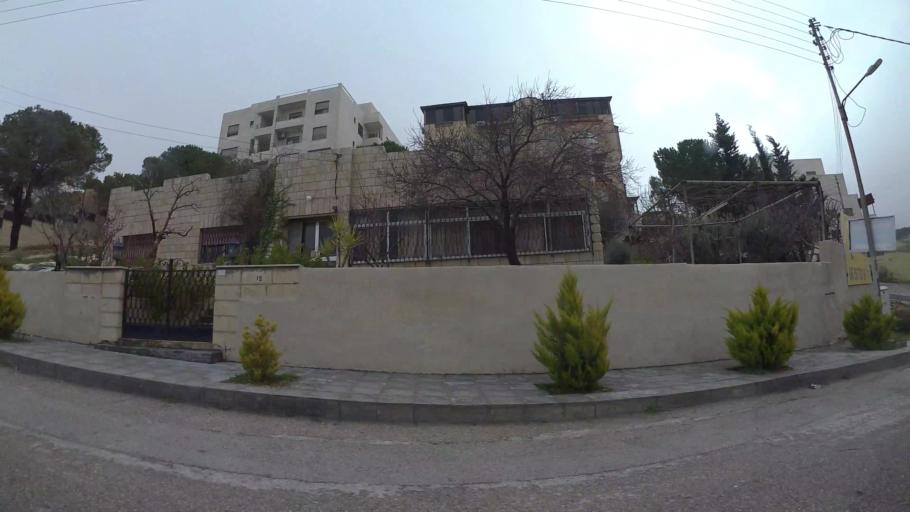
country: JO
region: Amman
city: Umm as Summaq
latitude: 31.9186
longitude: 35.8655
